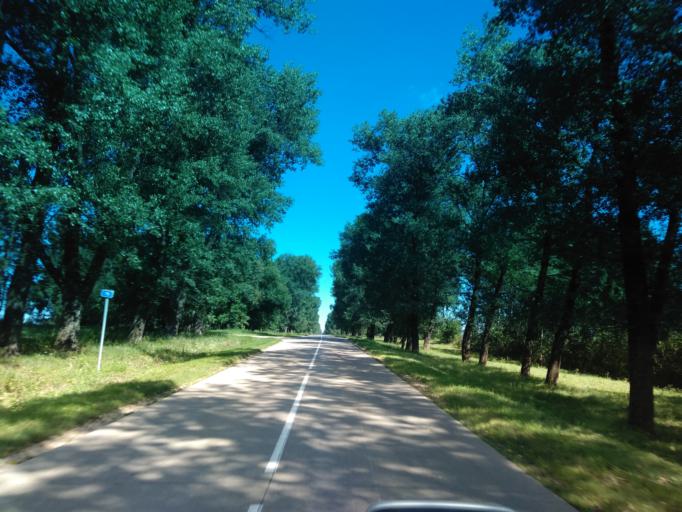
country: BY
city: Fanipol
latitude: 53.6749
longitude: 27.3517
